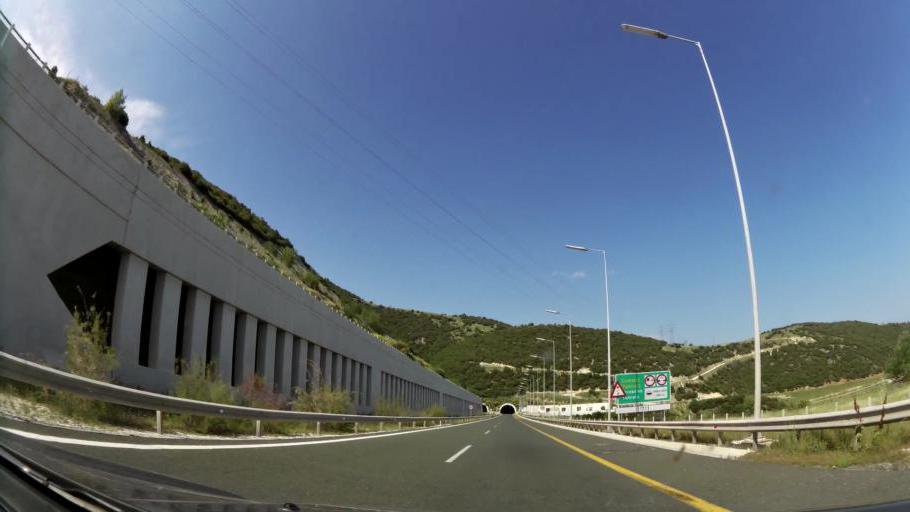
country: GR
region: West Macedonia
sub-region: Nomos Kozanis
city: Velventos
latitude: 40.3724
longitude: 22.0830
